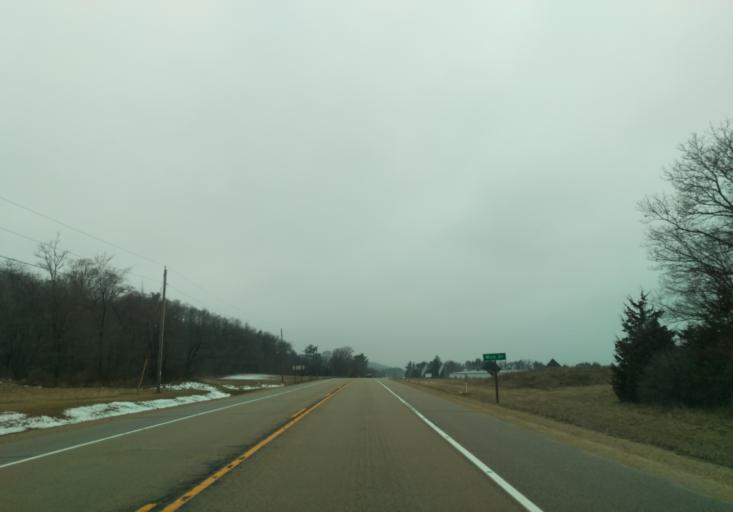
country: US
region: Wisconsin
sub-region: Dane County
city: Mazomanie
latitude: 43.1693
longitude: -89.8079
